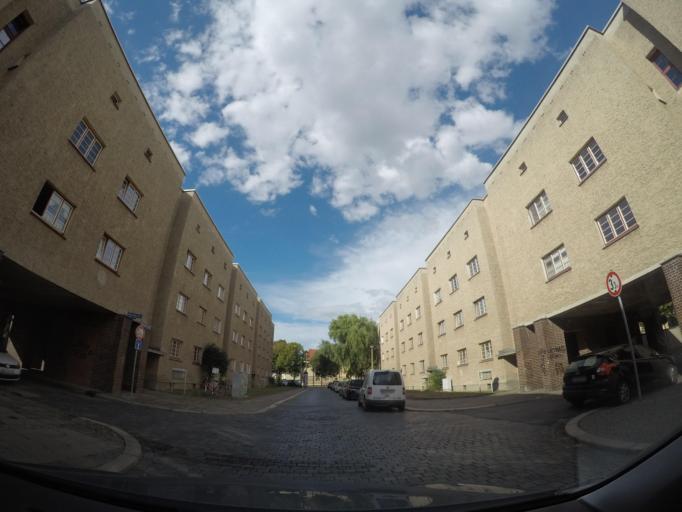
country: DE
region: Saxony-Anhalt
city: Diesdorf
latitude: 52.1280
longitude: 11.5875
